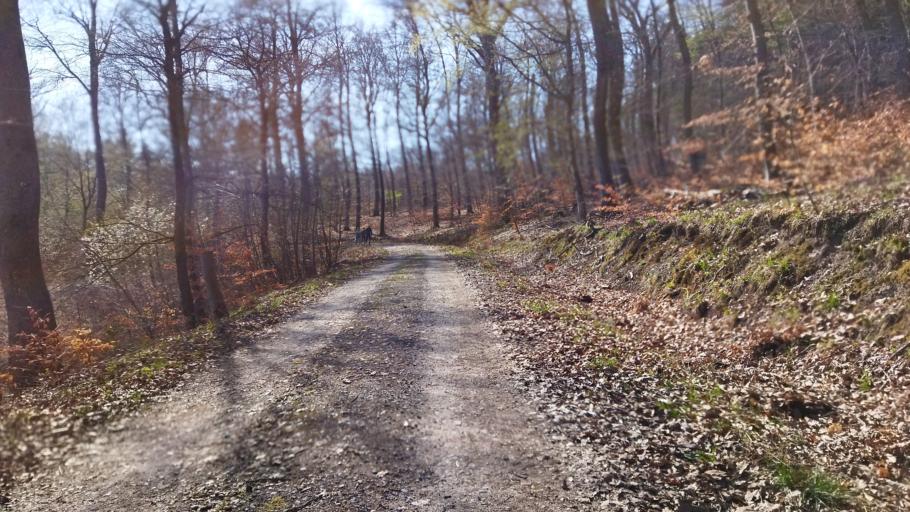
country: DE
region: Baden-Wuerttemberg
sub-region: Regierungsbezirk Stuttgart
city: Zaberfeld
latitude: 49.0311
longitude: 8.8907
